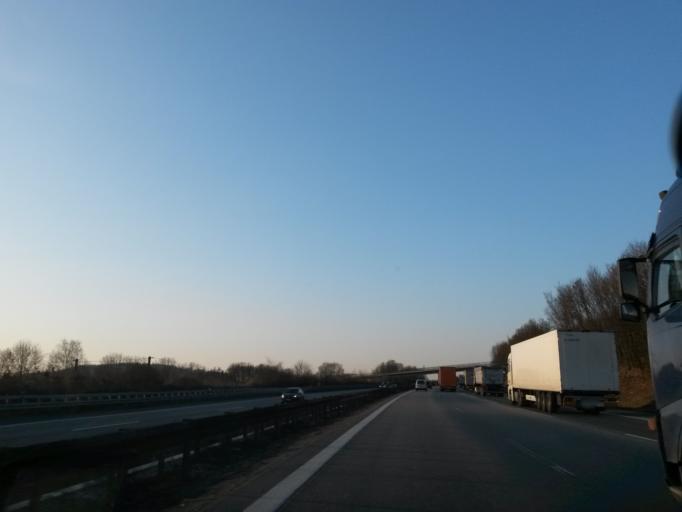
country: DE
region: Bavaria
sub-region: Regierungsbezirk Mittelfranken
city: Thalmassing
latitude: 49.1108
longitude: 11.2799
